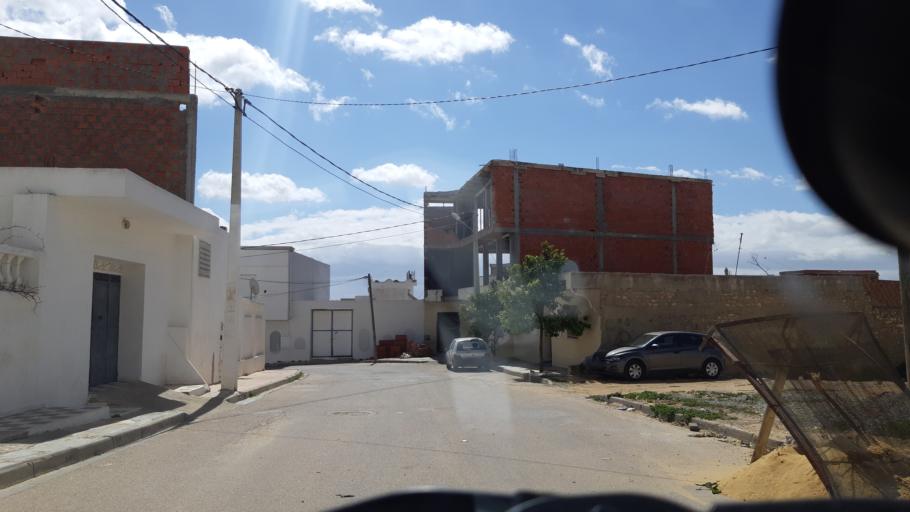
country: TN
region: Susah
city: Akouda
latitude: 35.8816
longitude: 10.5343
